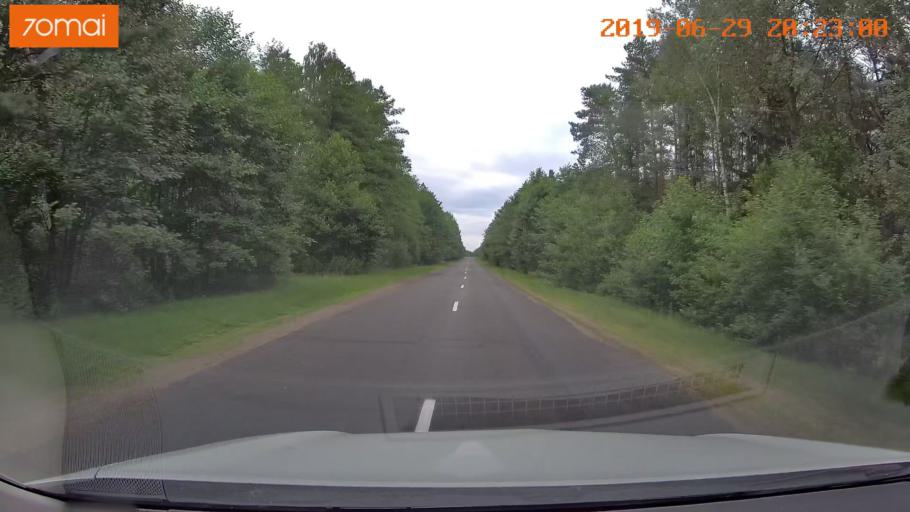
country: BY
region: Brest
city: Asnyezhytsy
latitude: 52.4388
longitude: 26.2578
